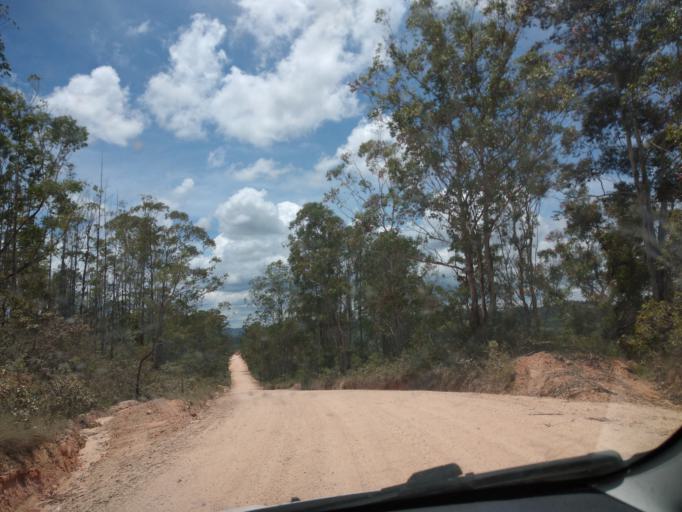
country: BR
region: Minas Gerais
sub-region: Tiradentes
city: Tiradentes
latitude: -20.9168
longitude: -44.2607
